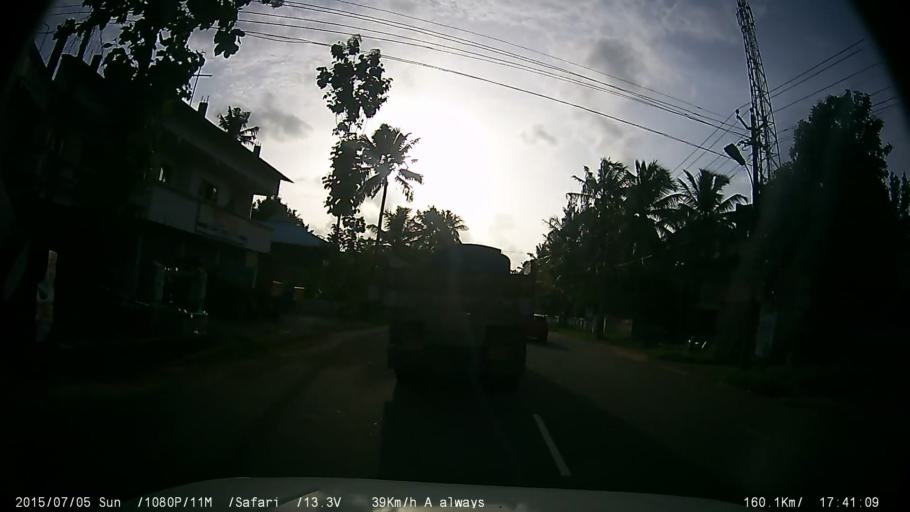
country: IN
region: Kerala
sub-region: Ernakulam
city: Angamali
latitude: 10.1817
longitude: 76.4123
